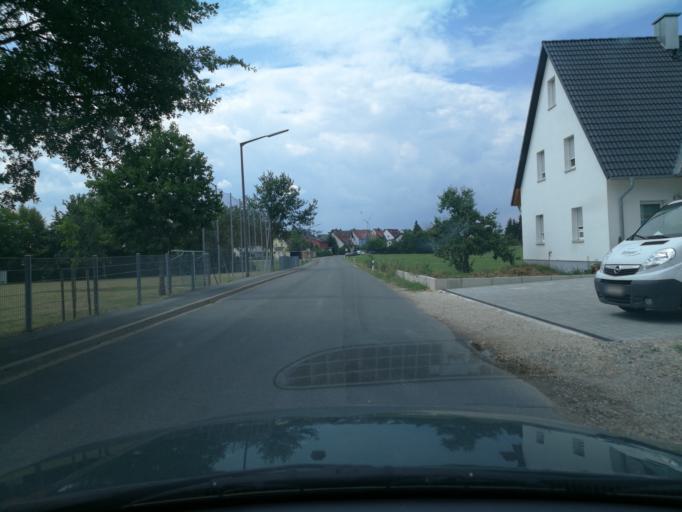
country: DE
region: Bavaria
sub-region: Regierungsbezirk Mittelfranken
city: Grosshabersdorf
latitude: 49.4396
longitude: 10.7957
